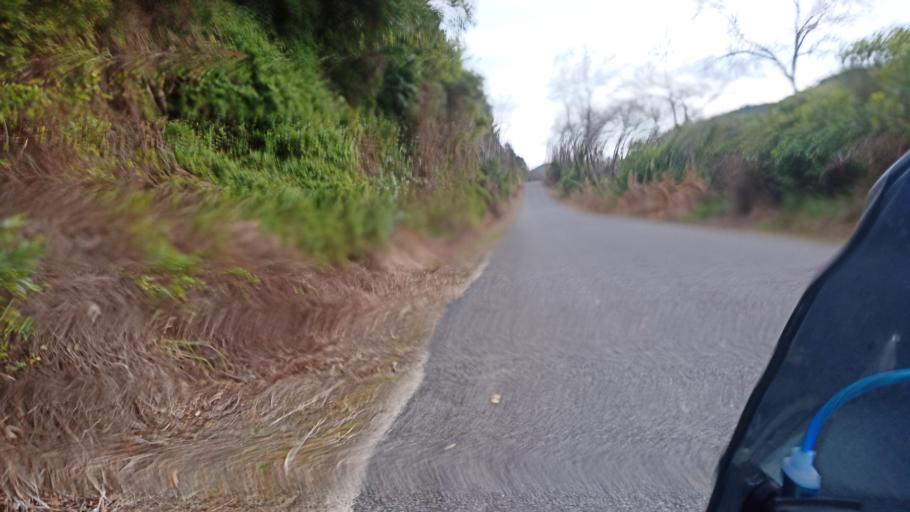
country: NZ
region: Hawke's Bay
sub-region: Wairoa District
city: Wairoa
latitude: -38.8232
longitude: 177.4981
